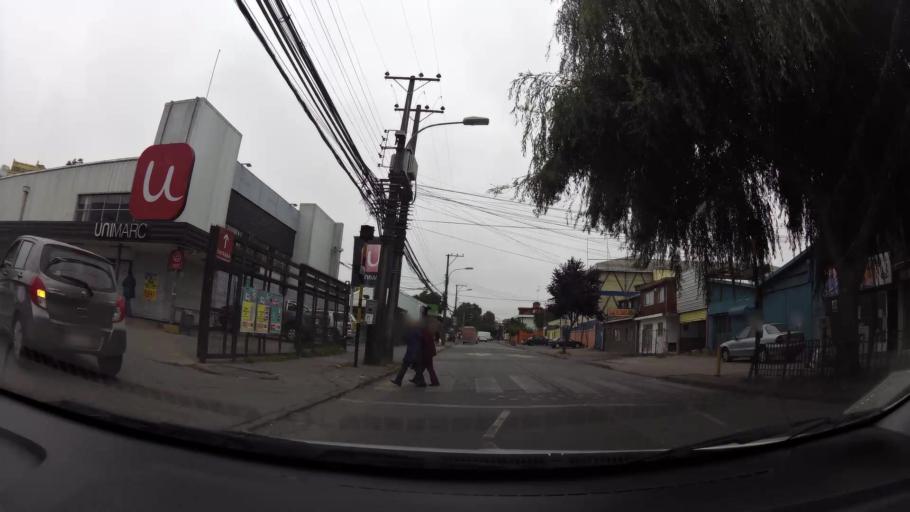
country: CL
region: Biobio
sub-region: Provincia de Concepcion
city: Concepcion
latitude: -36.8166
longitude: -73.0514
